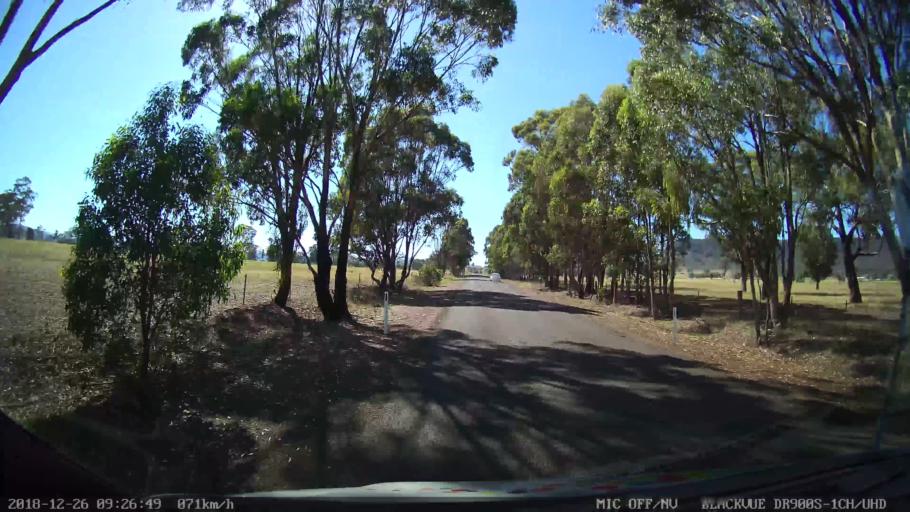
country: AU
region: New South Wales
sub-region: Mid-Western Regional
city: Kandos
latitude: -32.8309
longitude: 150.0115
